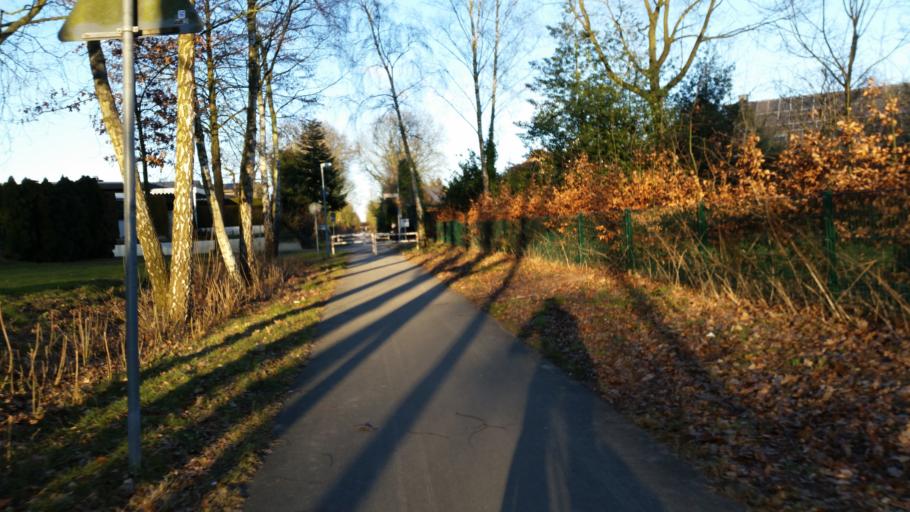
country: DE
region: North Rhine-Westphalia
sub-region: Regierungsbezirk Munster
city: Neuenkirchen
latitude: 52.2469
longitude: 7.3688
